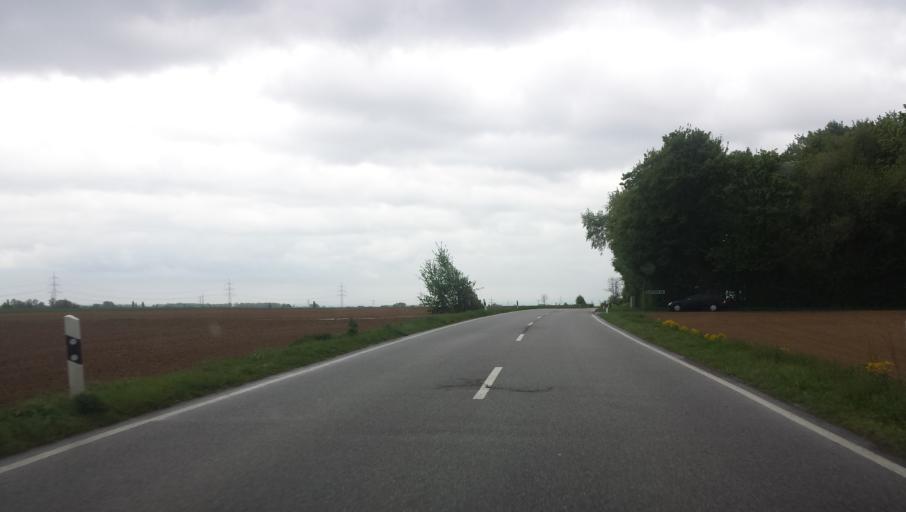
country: DE
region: Rheinland-Pfalz
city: Rulzheim
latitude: 49.1749
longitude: 8.2881
